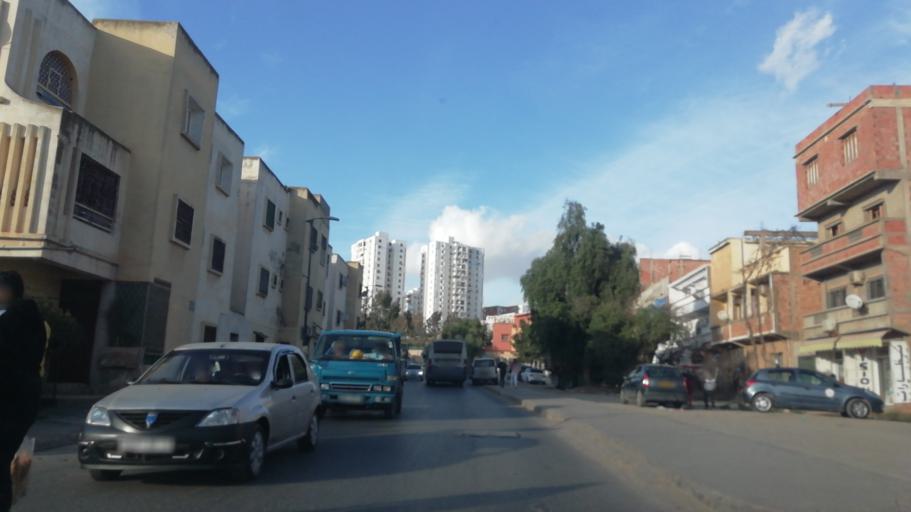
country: DZ
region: Oran
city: Bir el Djir
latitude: 35.6974
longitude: -0.5739
